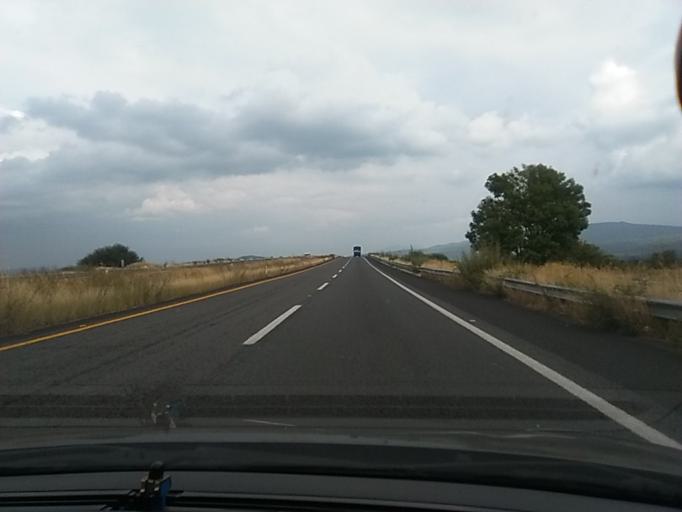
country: MX
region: Michoacan
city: Ecuandureo
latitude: 20.1766
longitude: -102.2471
